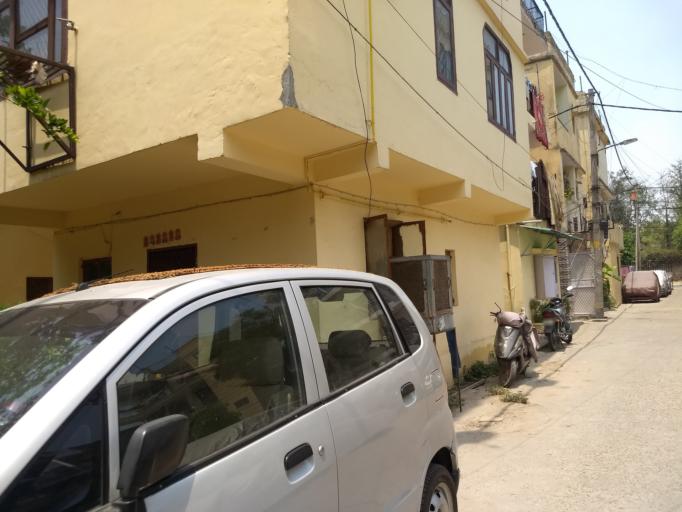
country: IN
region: NCT
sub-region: New Delhi
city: New Delhi
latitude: 28.5262
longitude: 77.1959
